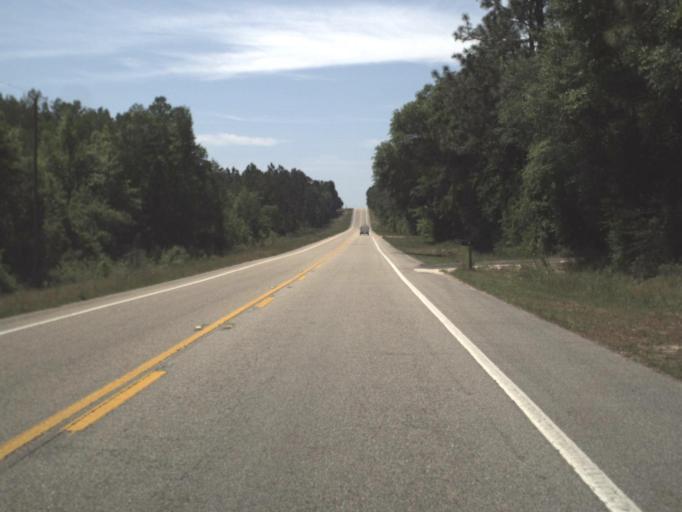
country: US
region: Florida
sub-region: Jackson County
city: Marianna
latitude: 30.6100
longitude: -85.1810
